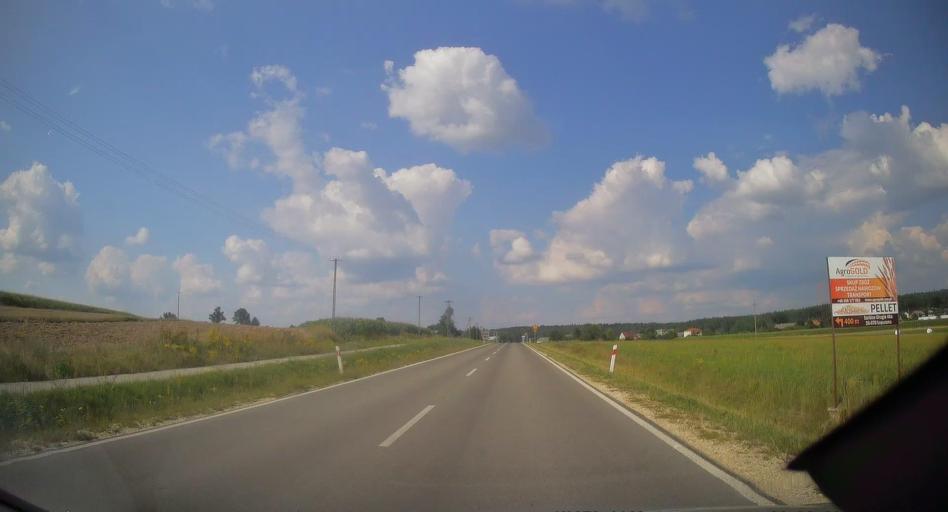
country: PL
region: Swietokrzyskie
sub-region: Powiat kielecki
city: Lopuszno
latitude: 50.9959
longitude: 20.2679
